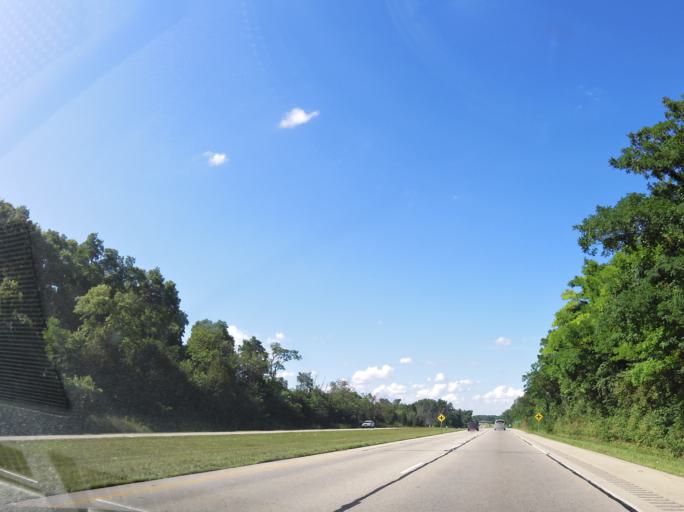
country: US
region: Ohio
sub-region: Greene County
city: Wright-Patterson AFB
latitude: 39.8318
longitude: -84.0622
